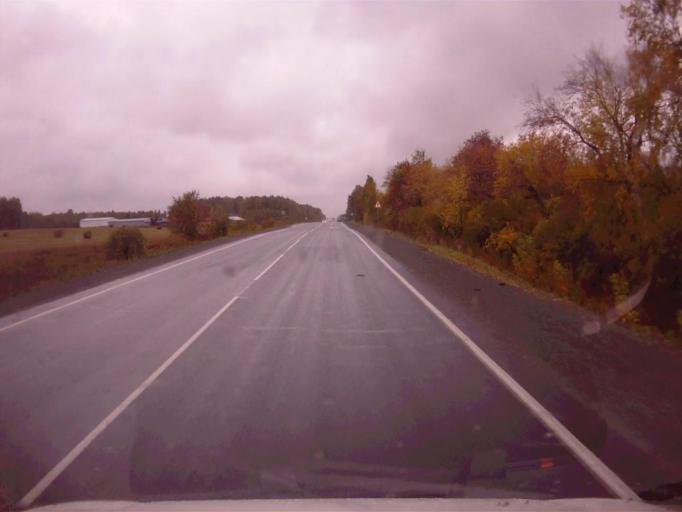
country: RU
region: Chelyabinsk
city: Novogornyy
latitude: 55.4891
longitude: 60.6917
